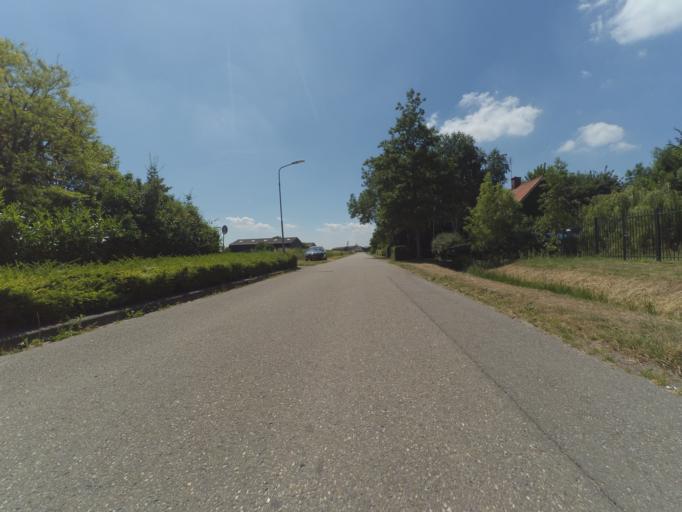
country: NL
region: Zeeland
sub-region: Gemeente Reimerswaal
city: Yerseke
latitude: 51.5487
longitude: 4.0682
